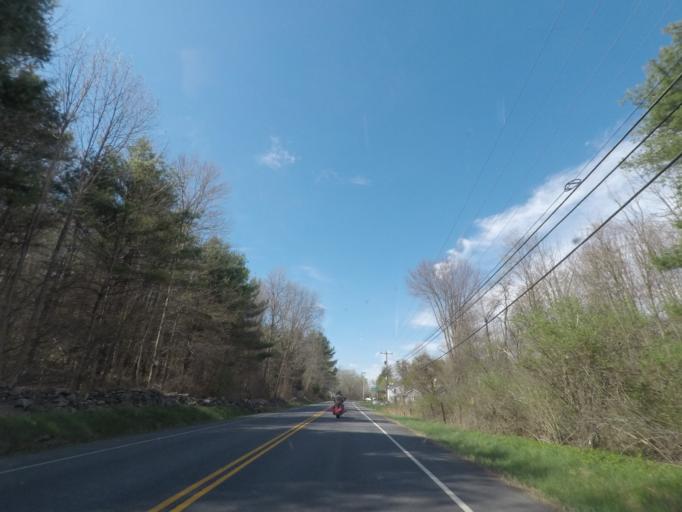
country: US
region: New York
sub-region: Greene County
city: Cairo
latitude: 42.3547
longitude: -74.0485
